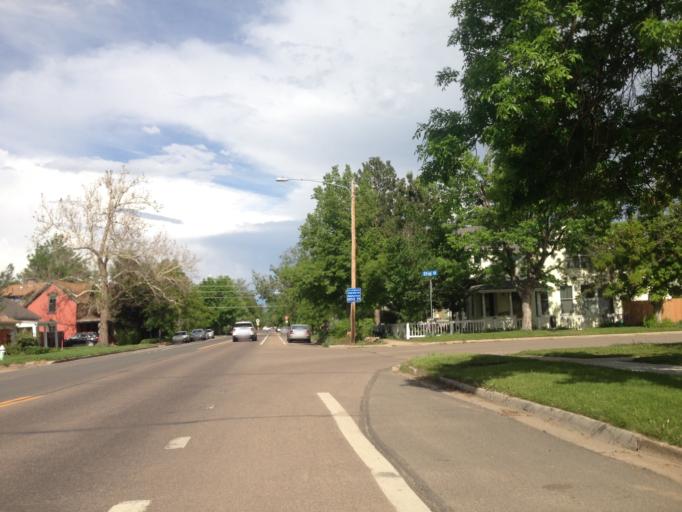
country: US
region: Colorado
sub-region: Boulder County
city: Boulder
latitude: 40.0225
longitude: -105.2680
